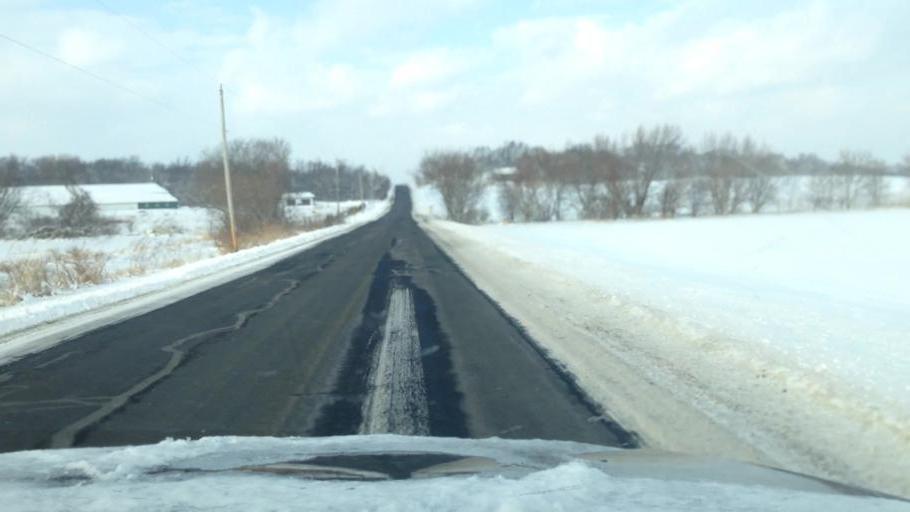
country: US
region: Wisconsin
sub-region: Walworth County
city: East Troy
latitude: 42.7697
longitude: -88.4453
